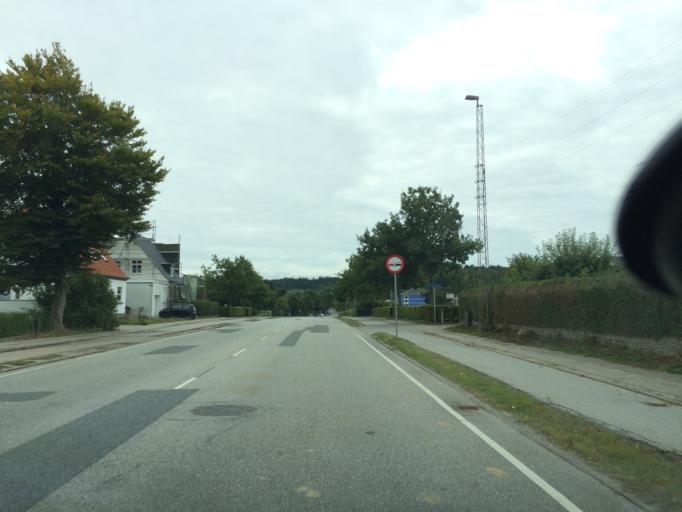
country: DK
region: South Denmark
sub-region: Aabenraa Kommune
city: Aabenraa
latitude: 55.0313
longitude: 9.4087
